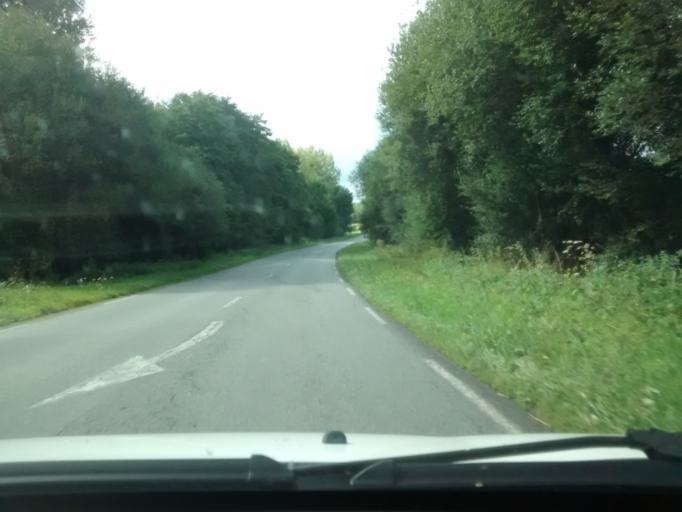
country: FR
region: Brittany
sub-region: Departement d'Ille-et-Vilaine
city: Plerguer
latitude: 48.5127
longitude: -1.8607
